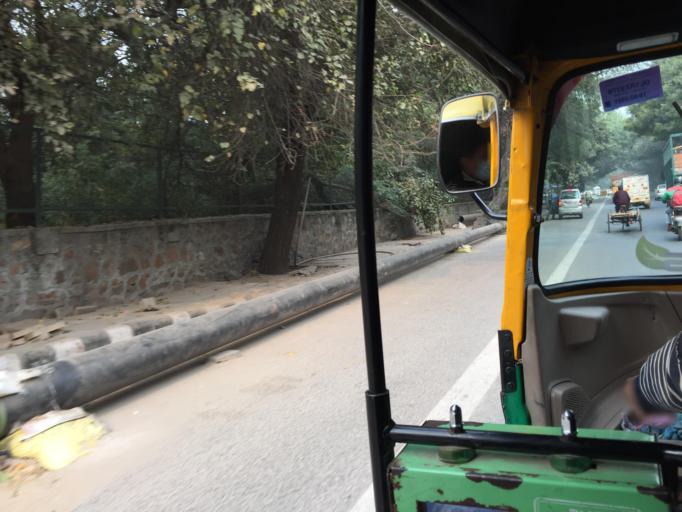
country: IN
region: NCT
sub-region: New Delhi
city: New Delhi
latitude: 28.5149
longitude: 77.1870
